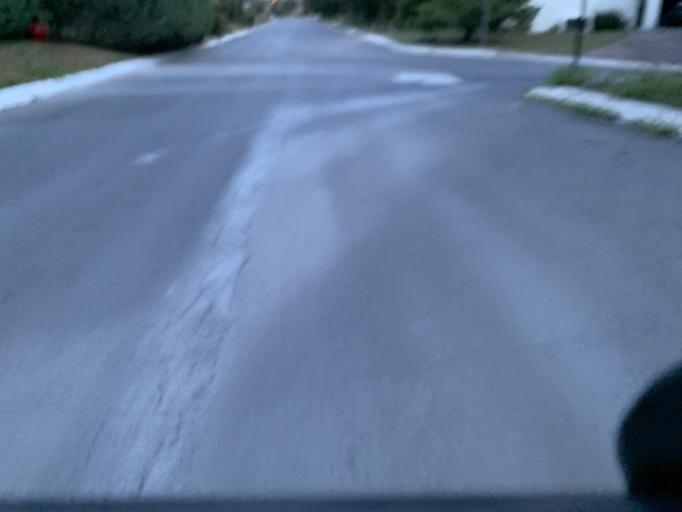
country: MX
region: Nuevo Leon
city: Santiago
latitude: 25.5067
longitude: -100.1874
